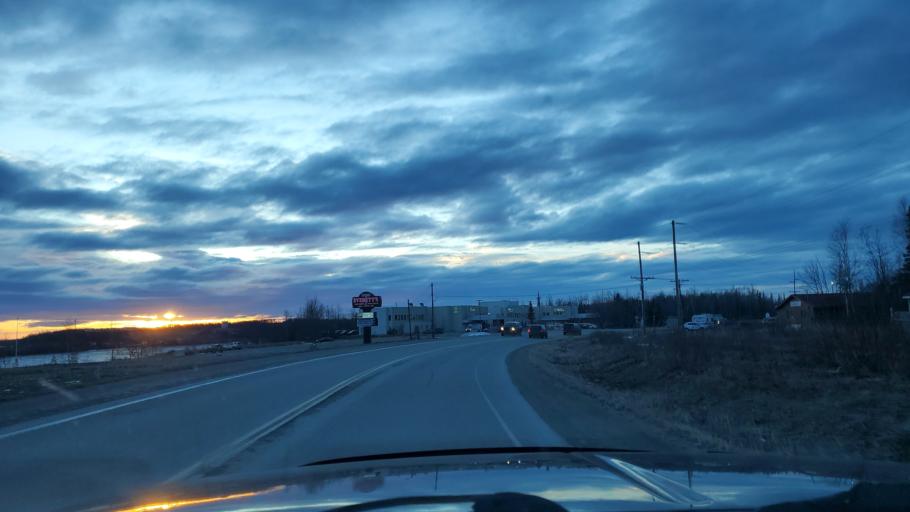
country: US
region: Alaska
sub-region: Matanuska-Susitna Borough
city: Wasilla
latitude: 61.5895
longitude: -149.4022
